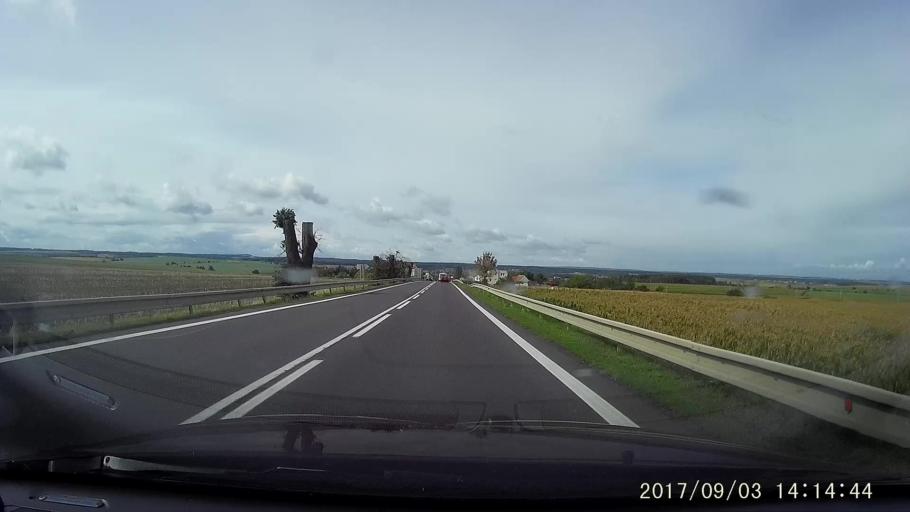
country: CZ
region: South Moravian
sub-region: Okres Znojmo
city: Znojmo
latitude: 48.8869
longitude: 16.0030
